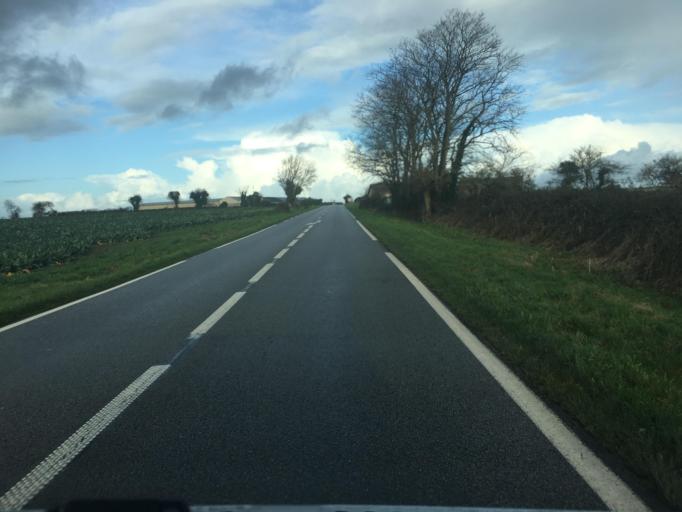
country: FR
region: Lower Normandy
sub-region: Departement de la Manche
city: Reville
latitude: 49.6402
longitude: -1.2847
